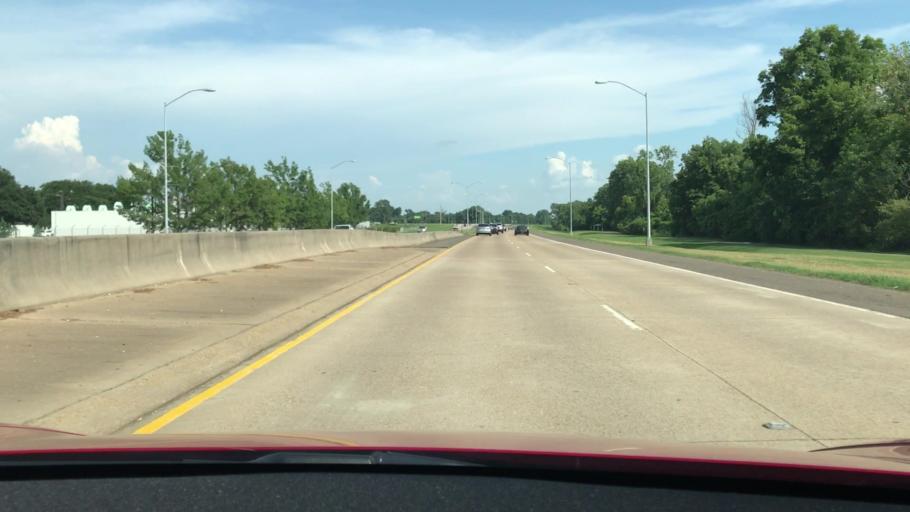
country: US
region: Louisiana
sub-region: Bossier Parish
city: Bossier City
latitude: 32.4832
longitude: -93.6855
